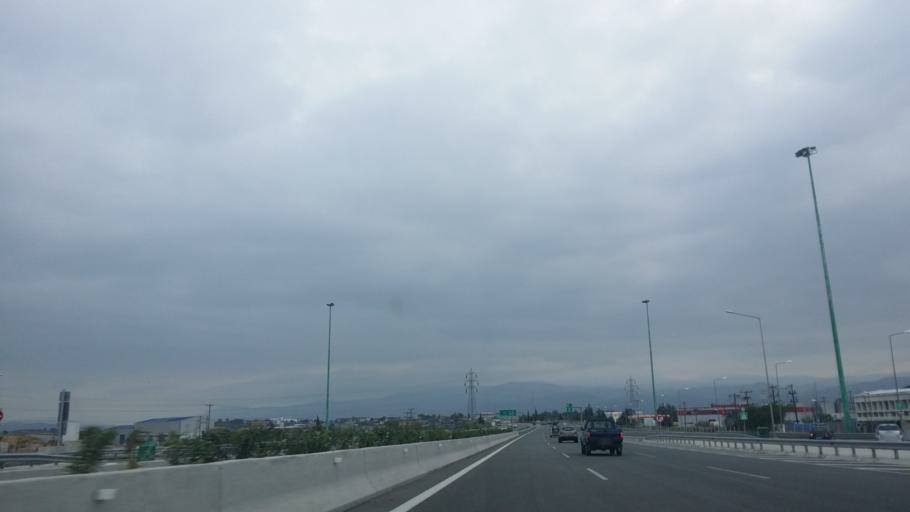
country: GR
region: Central Greece
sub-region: Nomos Voiotias
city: Schimatari
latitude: 38.3346
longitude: 23.5997
